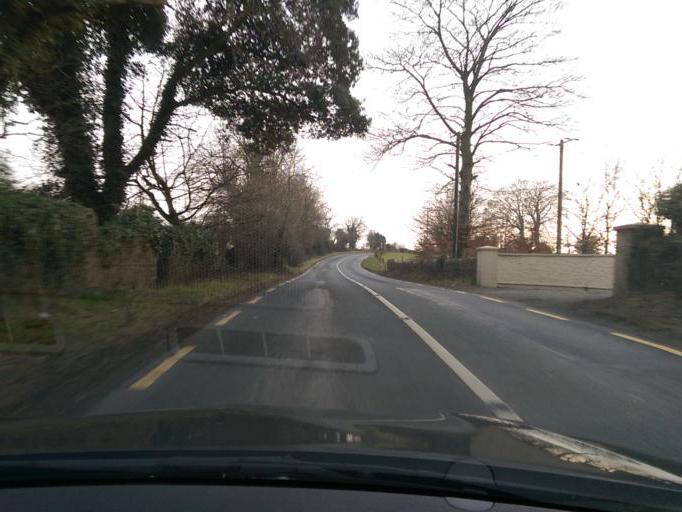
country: IE
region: Leinster
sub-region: An Longfort
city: Ballymahon
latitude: 53.5011
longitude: -7.8430
